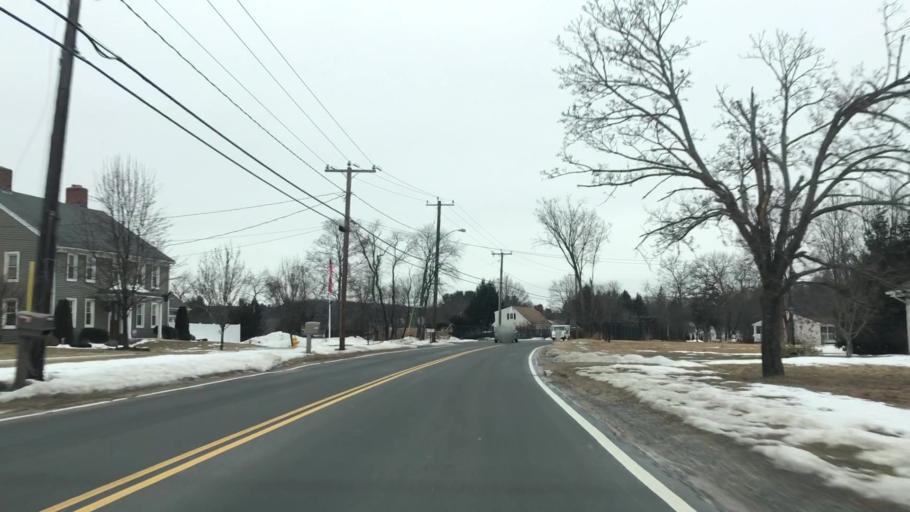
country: US
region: Massachusetts
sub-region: Hampden County
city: West Springfield
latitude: 42.0875
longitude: -72.6825
